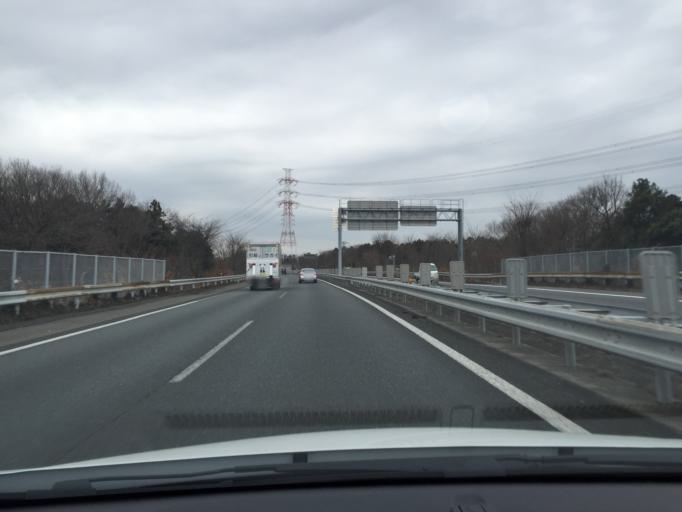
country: JP
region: Saitama
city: Sakado
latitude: 35.9175
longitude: 139.3873
